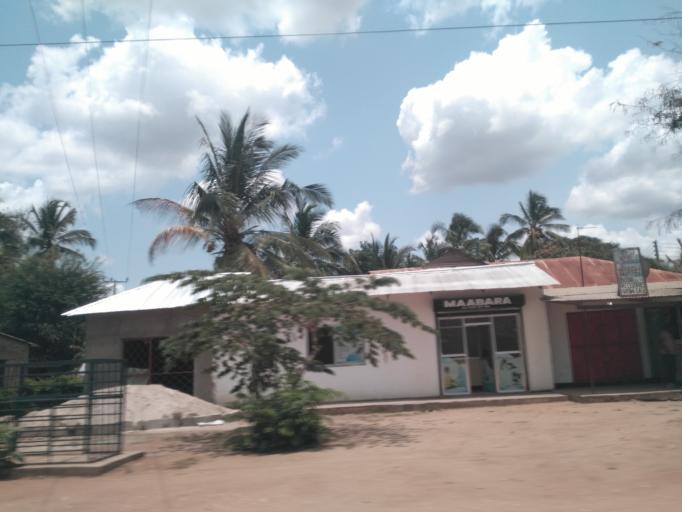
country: TZ
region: Dar es Salaam
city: Dar es Salaam
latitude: -6.8475
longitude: 39.3541
